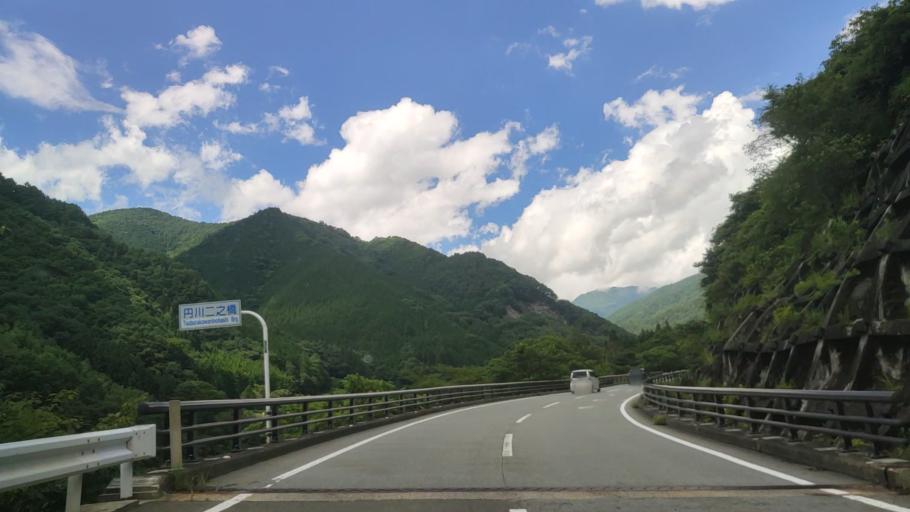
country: JP
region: Yamanashi
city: Enzan
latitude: 35.8187
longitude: 138.7572
